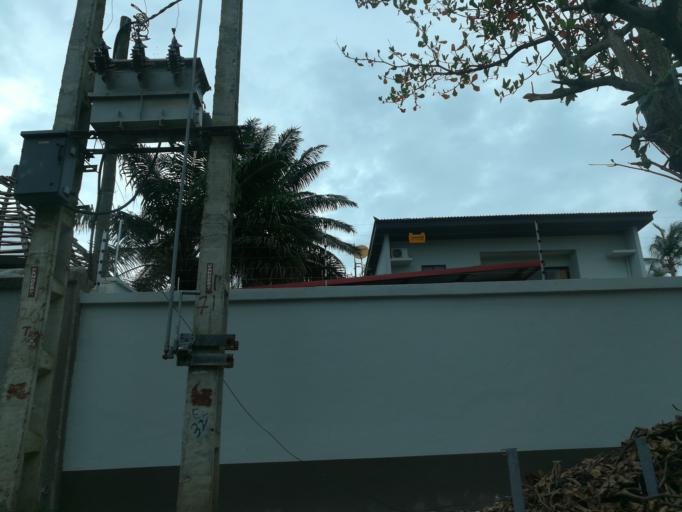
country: NG
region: Lagos
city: Lagos
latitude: 6.4350
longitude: 3.4113
